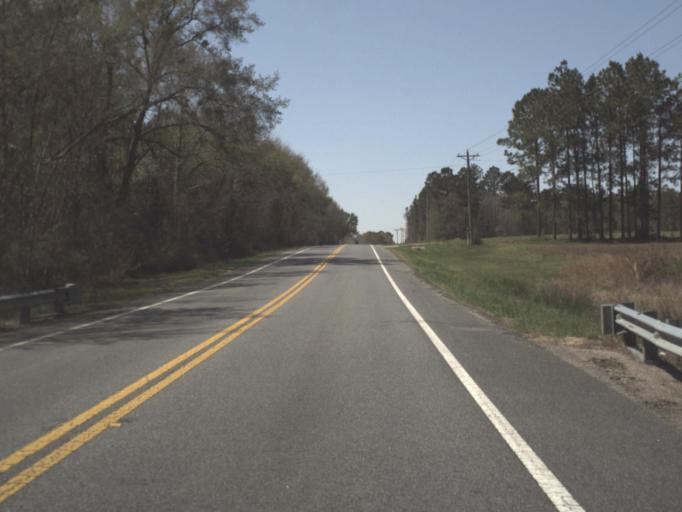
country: US
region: Alabama
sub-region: Geneva County
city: Geneva
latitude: 30.9547
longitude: -85.9120
